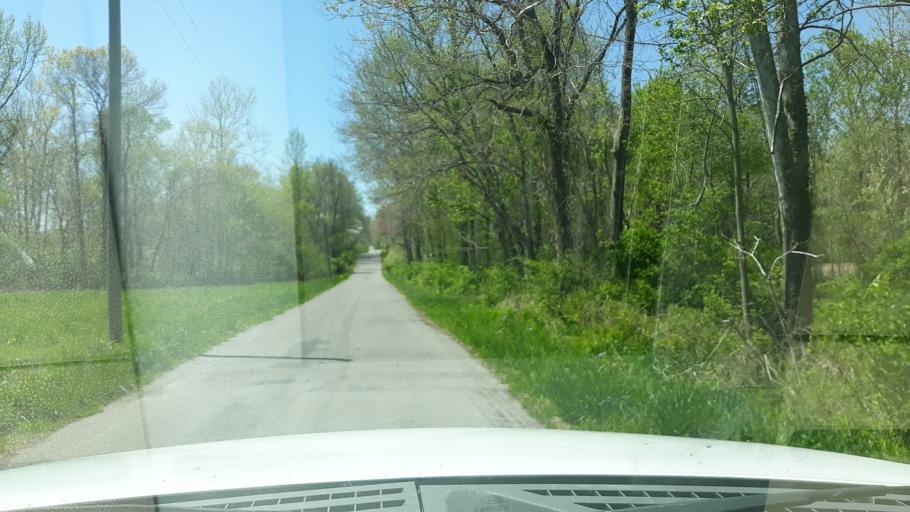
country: US
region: Illinois
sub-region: Saline County
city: Harrisburg
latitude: 37.8595
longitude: -88.6220
